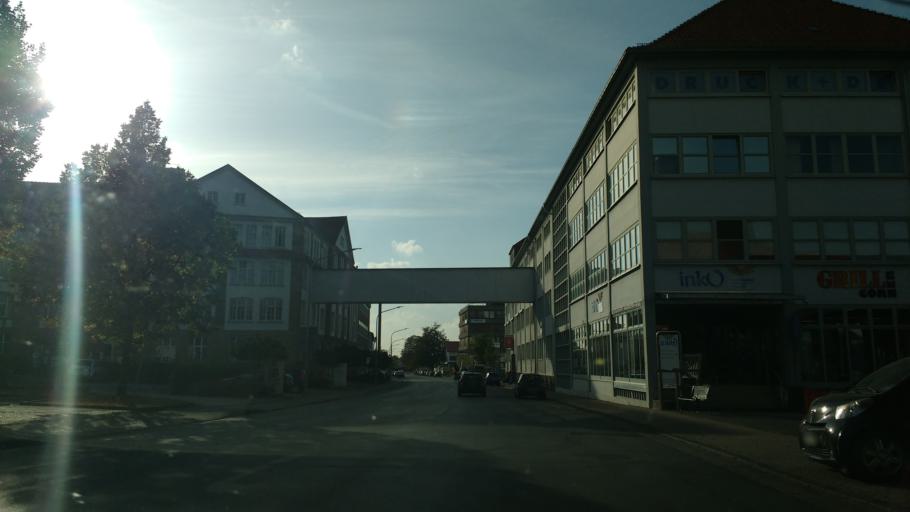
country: DE
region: North Rhine-Westphalia
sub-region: Regierungsbezirk Detmold
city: Lemgo
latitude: 52.0232
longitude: 8.8941
